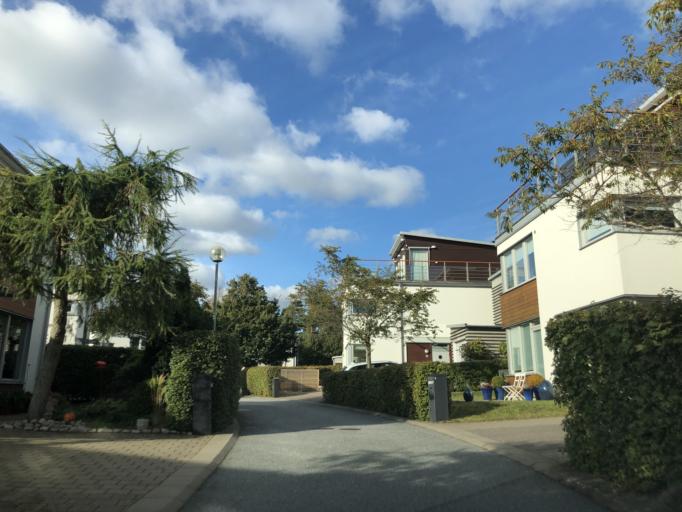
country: SE
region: Vaestra Goetaland
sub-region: Goteborg
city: Billdal
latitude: 57.6265
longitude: 11.9499
